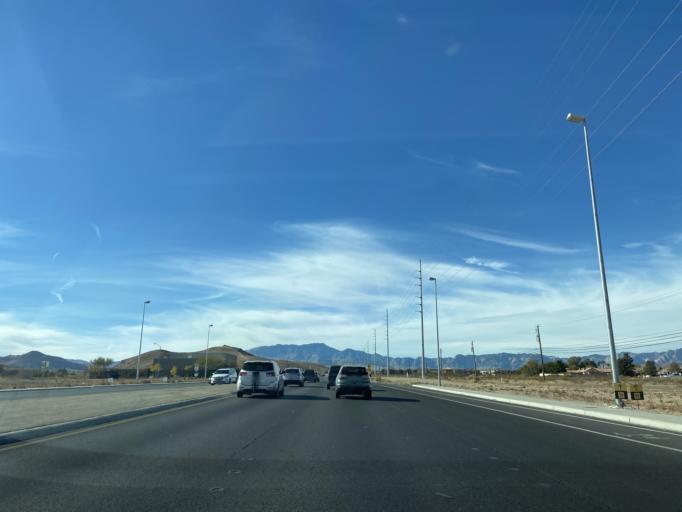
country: US
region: Nevada
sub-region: Clark County
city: Enterprise
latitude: 36.0220
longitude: -115.2461
